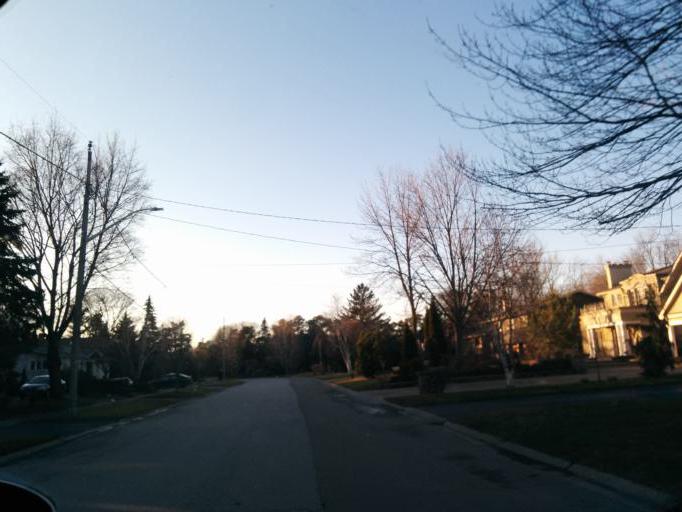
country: CA
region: Ontario
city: Mississauga
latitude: 43.5588
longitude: -79.6194
